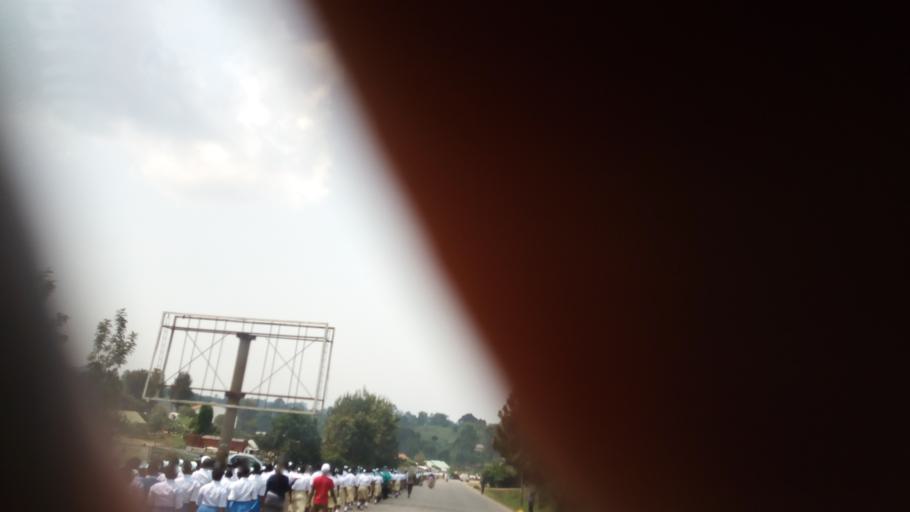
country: UG
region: Western Region
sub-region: Rukungiri District
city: Rukungiri
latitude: -0.7941
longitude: 29.9282
